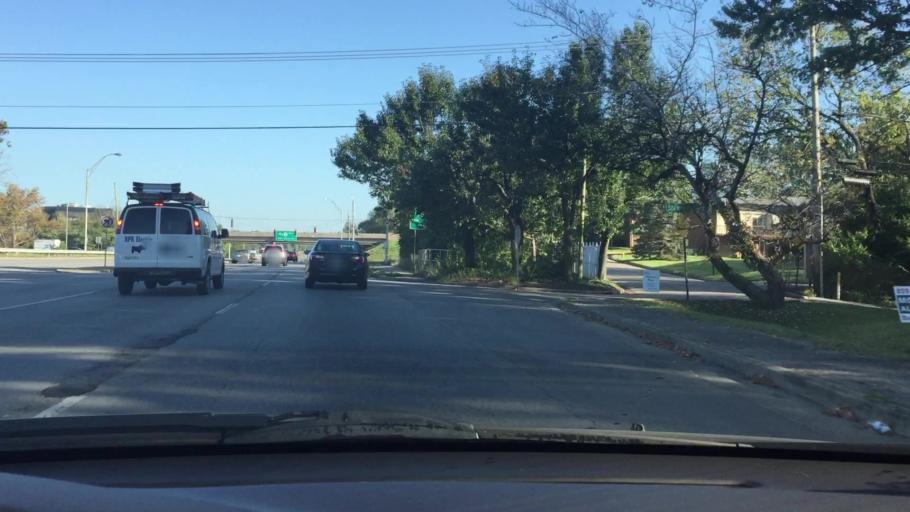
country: US
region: Kentucky
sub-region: Fayette County
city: Lexington
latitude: 37.9889
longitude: -84.4945
